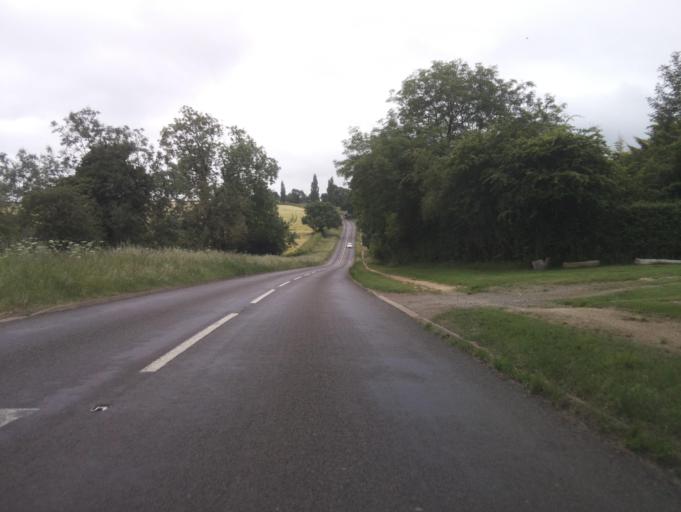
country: GB
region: England
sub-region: District of Rutland
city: Preston
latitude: 52.6050
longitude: -0.7196
